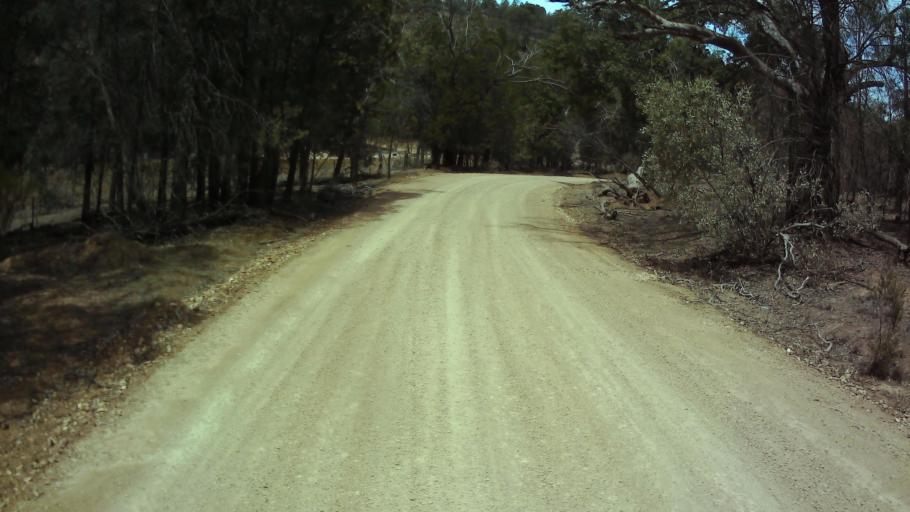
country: AU
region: New South Wales
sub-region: Weddin
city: Grenfell
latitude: -33.8144
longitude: 148.1638
